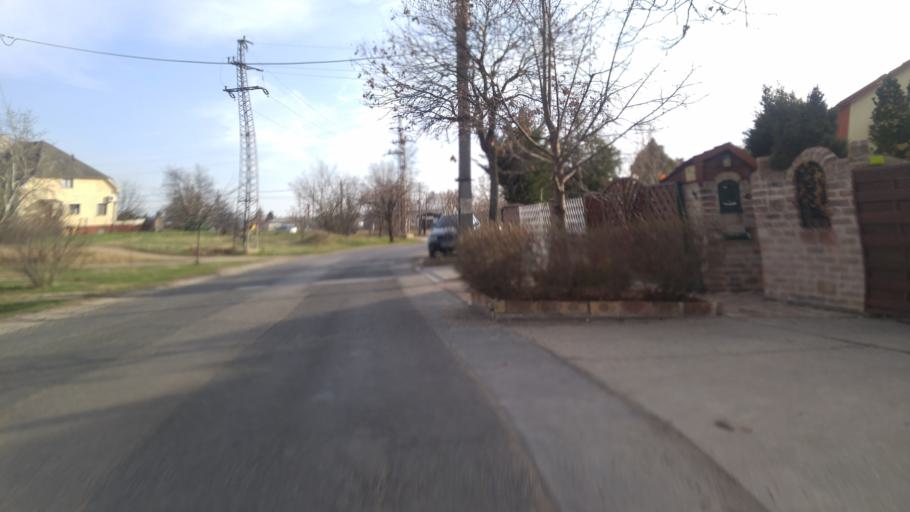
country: HU
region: Budapest
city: Budapest XVII. keruelet
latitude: 47.4762
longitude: 19.2391
